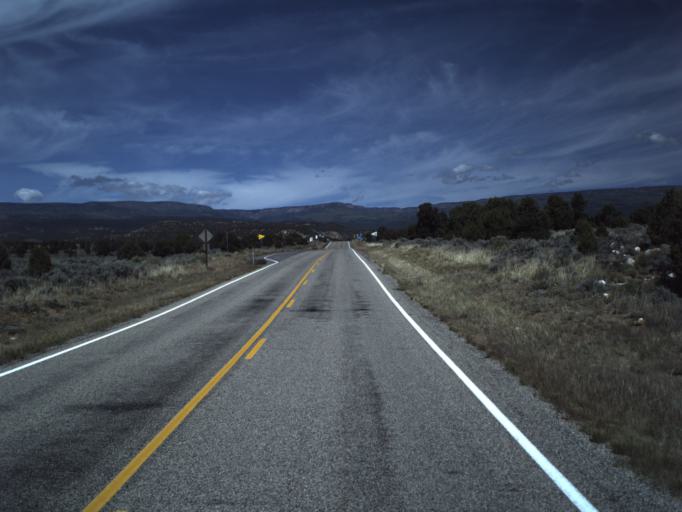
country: US
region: Utah
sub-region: Wayne County
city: Loa
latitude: 37.8820
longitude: -111.4576
